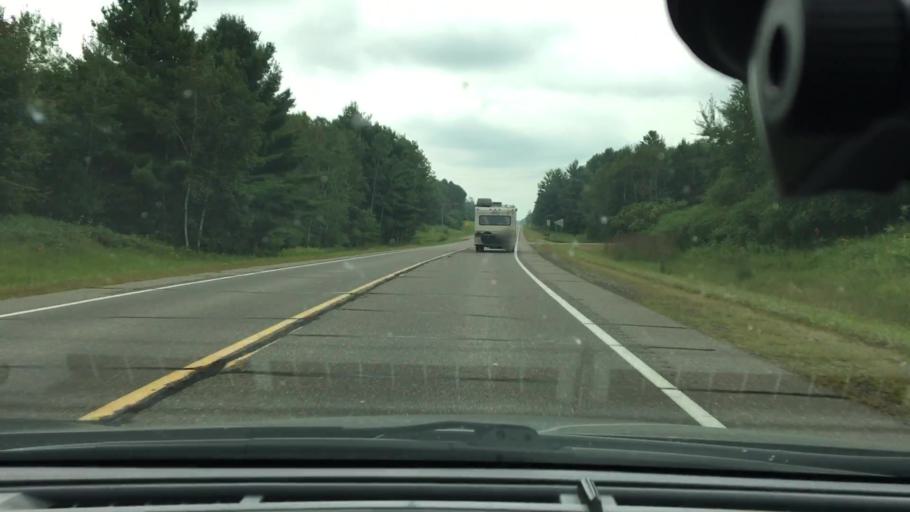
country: US
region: Minnesota
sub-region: Crow Wing County
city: Crosby
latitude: 46.4344
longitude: -93.8737
